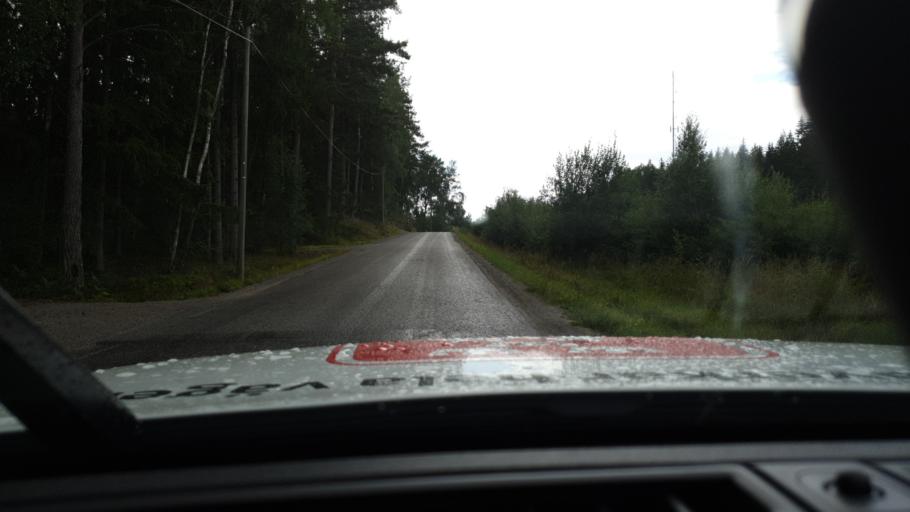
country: SE
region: Stockholm
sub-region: Nynashamns Kommun
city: Osmo
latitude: 59.0308
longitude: 17.9288
